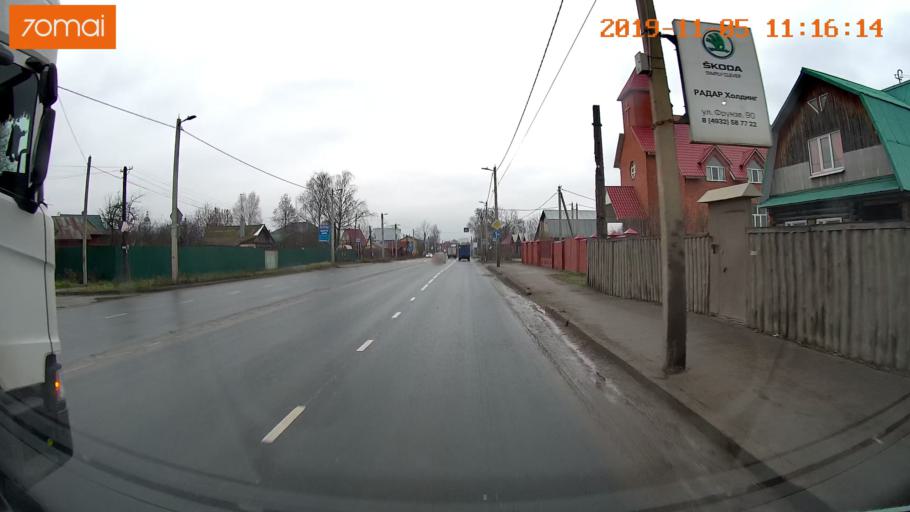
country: RU
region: Ivanovo
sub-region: Gorod Ivanovo
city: Ivanovo
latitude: 56.9831
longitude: 40.9536
